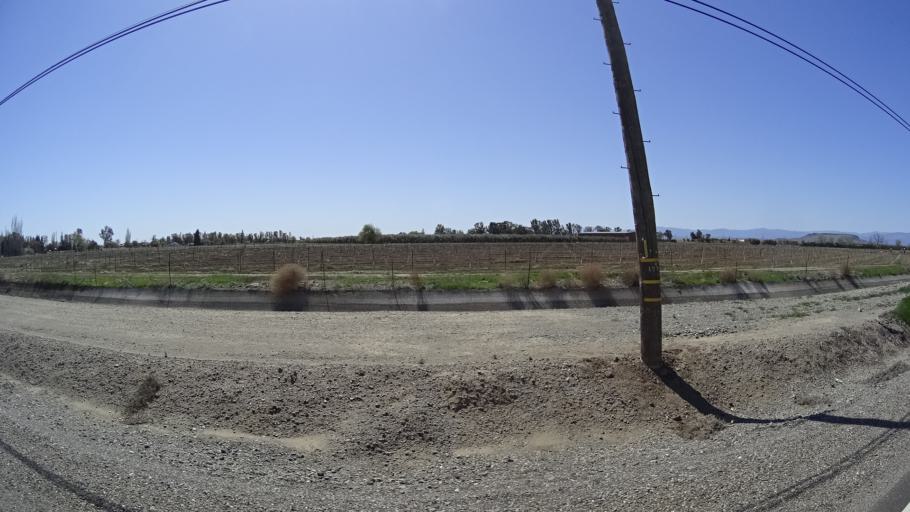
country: US
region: California
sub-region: Glenn County
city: Orland
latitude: 39.7641
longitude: -122.2402
